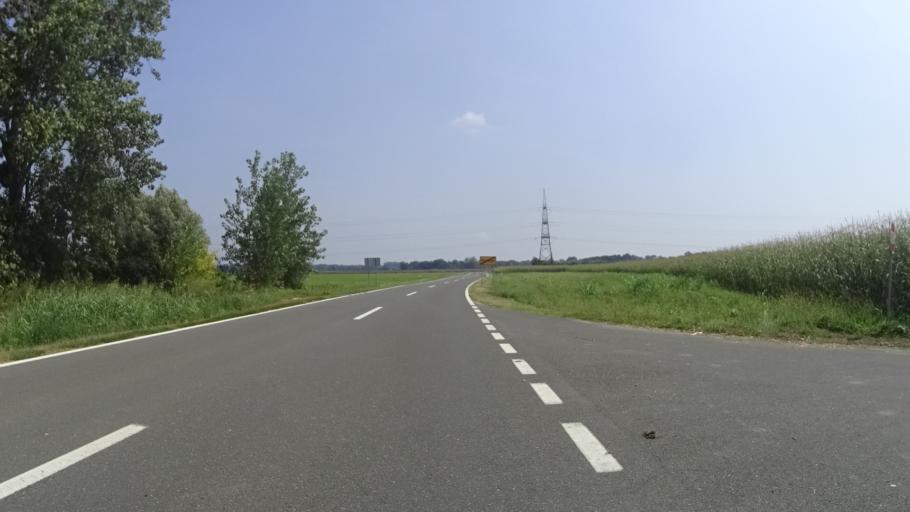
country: HR
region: Medimurska
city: Hodosan
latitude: 46.3978
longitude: 16.6474
